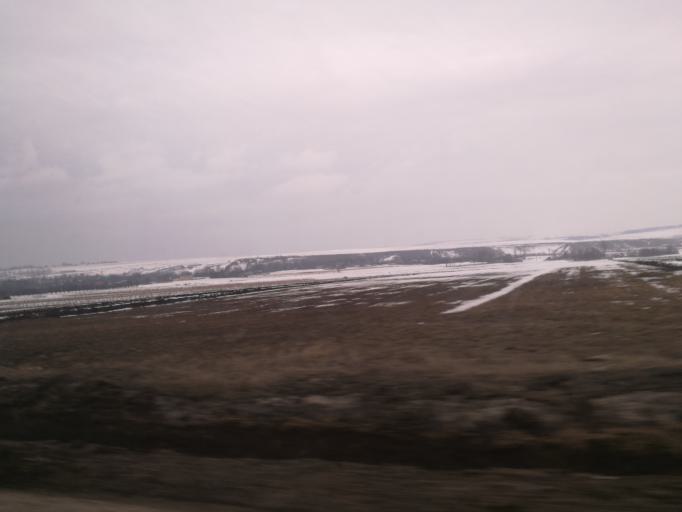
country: RO
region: Iasi
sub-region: Comuna Ruginoasa
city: Dumbravita
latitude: 47.2370
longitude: 26.8207
